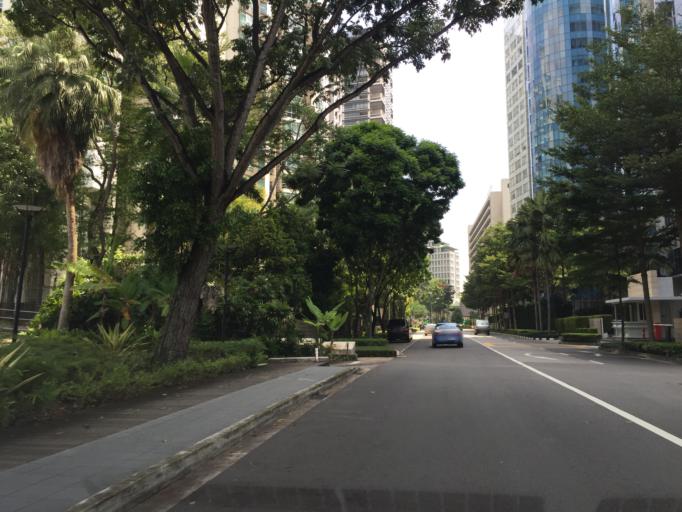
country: SG
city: Singapore
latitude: 1.3055
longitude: 103.8271
